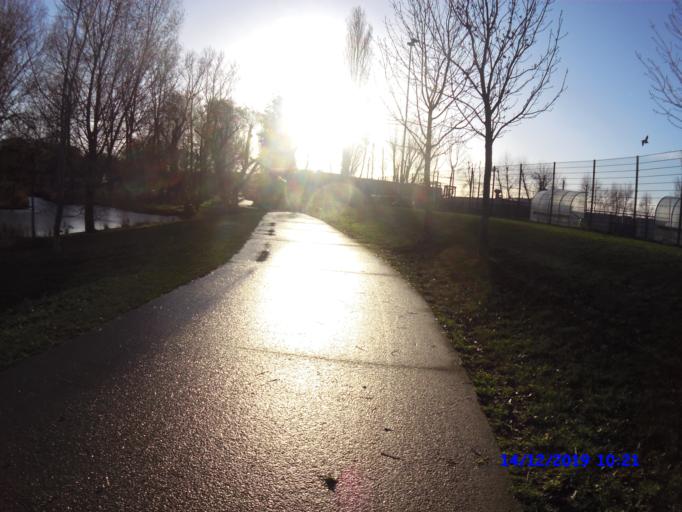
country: BE
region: Flanders
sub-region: Provincie Vlaams-Brabant
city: Drogenbos
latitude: 50.8024
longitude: 4.3118
